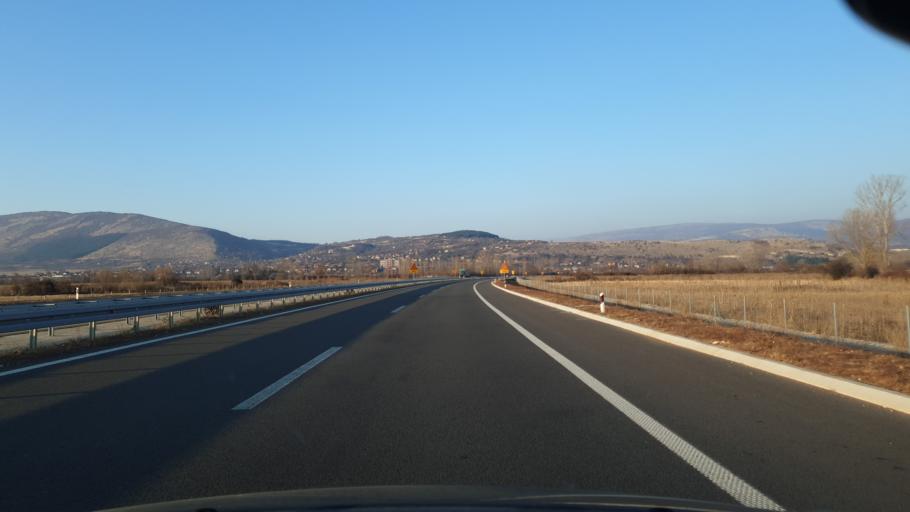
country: RS
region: Central Serbia
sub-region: Pirotski Okrug
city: Pirot
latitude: 43.1429
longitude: 22.5677
